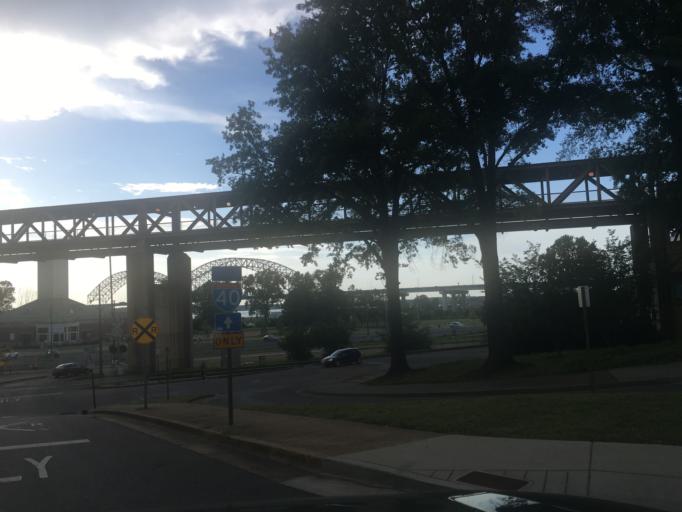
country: US
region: Tennessee
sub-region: Shelby County
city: Memphis
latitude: 35.1486
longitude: -90.0530
